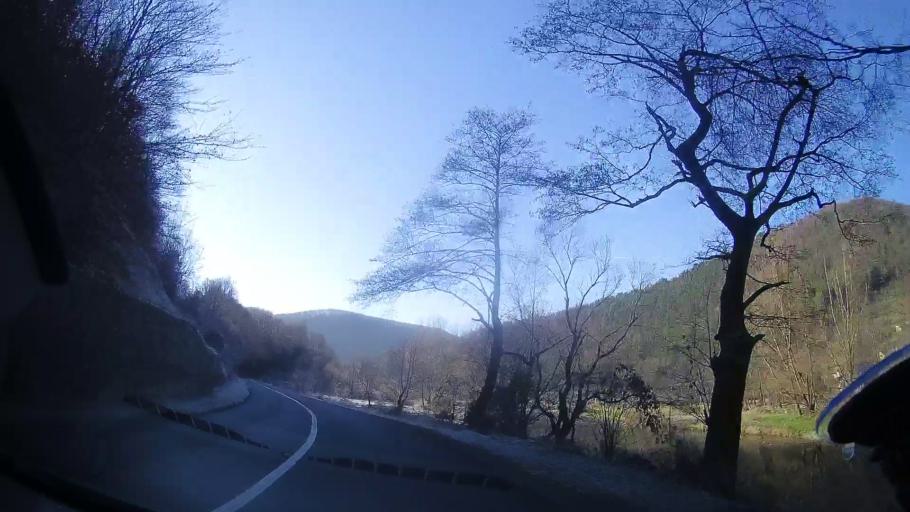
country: RO
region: Bihor
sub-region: Comuna Bulz
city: Bulz
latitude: 46.9312
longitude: 22.6623
